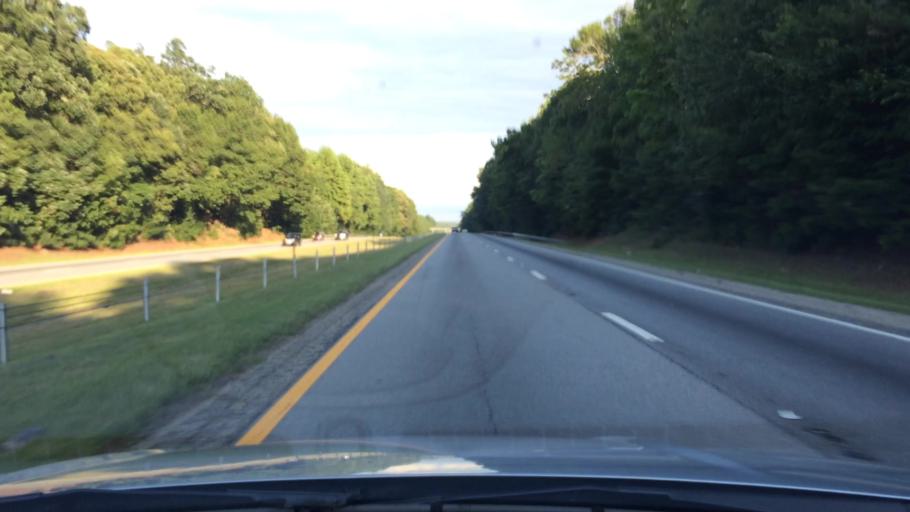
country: US
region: South Carolina
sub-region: Lexington County
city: Chapin
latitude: 34.1978
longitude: -81.3592
